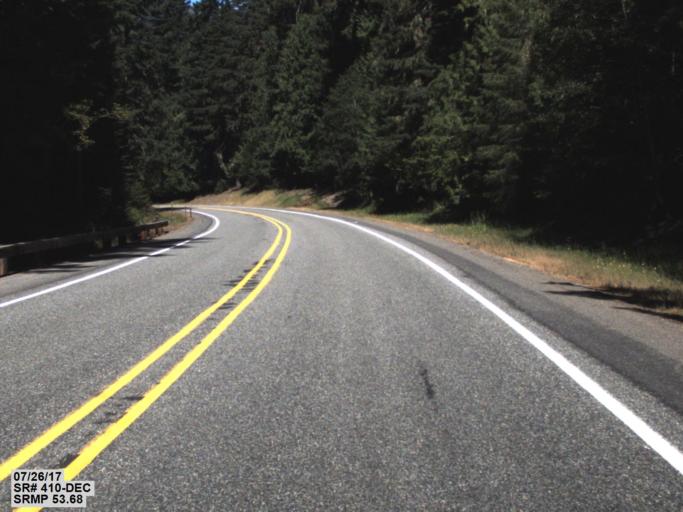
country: US
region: Washington
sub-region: King County
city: Enumclaw
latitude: 47.0289
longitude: -121.5466
